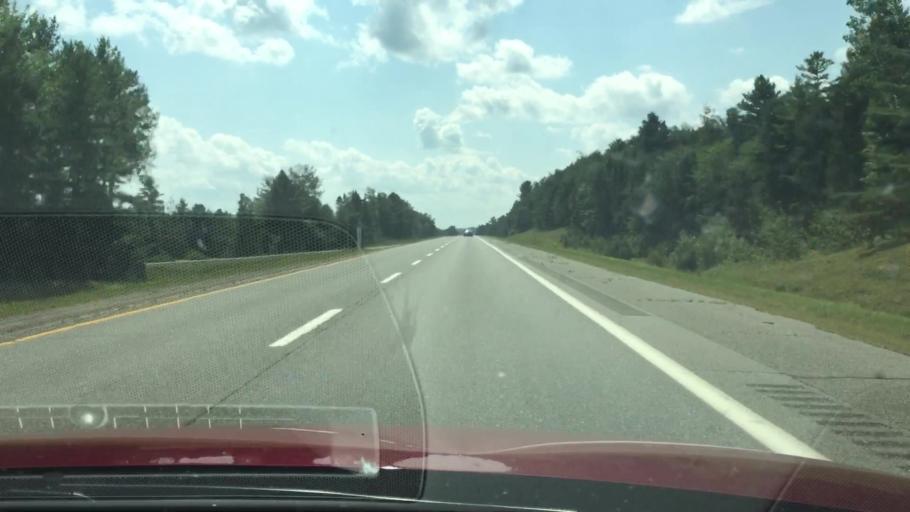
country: US
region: Maine
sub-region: Penobscot County
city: Medway
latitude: 45.4979
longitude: -68.5610
